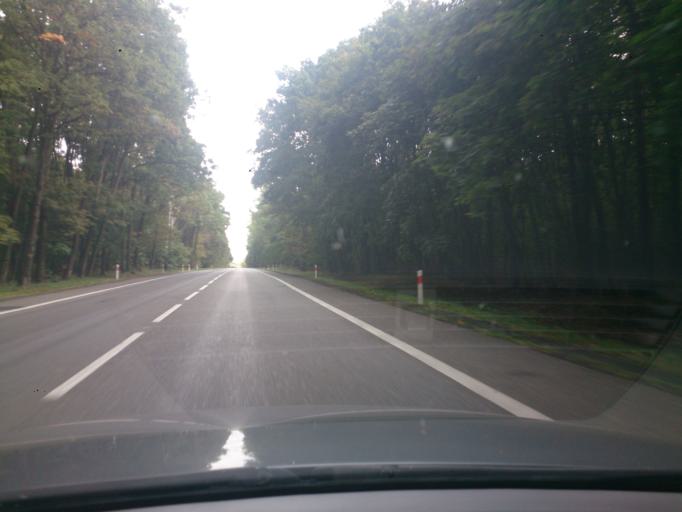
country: PL
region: Kujawsko-Pomorskie
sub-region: Powiat swiecki
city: Jezewo
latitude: 53.4444
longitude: 18.5594
